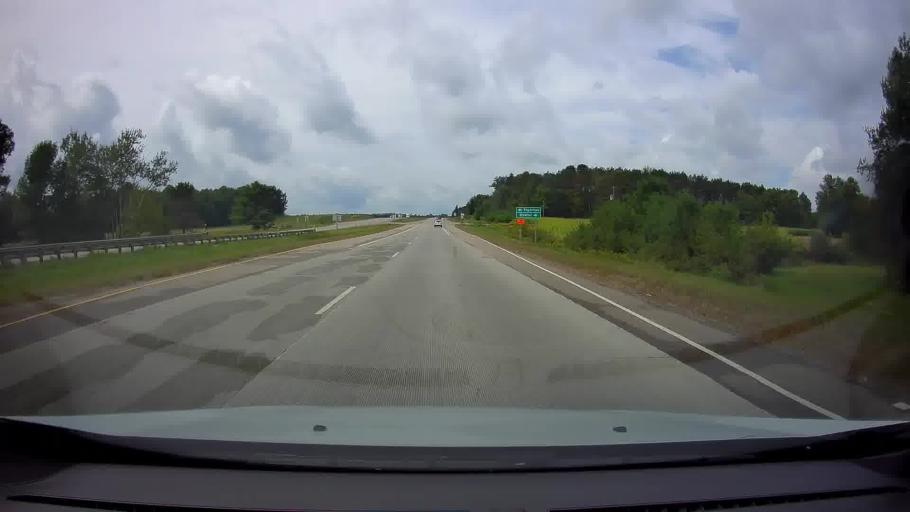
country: US
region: Wisconsin
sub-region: Shawano County
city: Wittenberg
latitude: 44.8039
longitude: -89.0172
